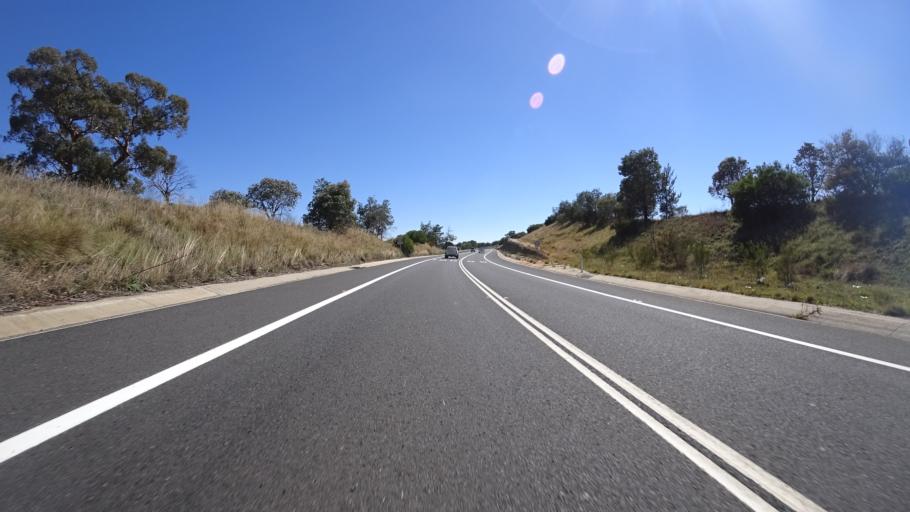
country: AU
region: New South Wales
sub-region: Lithgow
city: Portland
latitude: -33.3929
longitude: 150.0792
